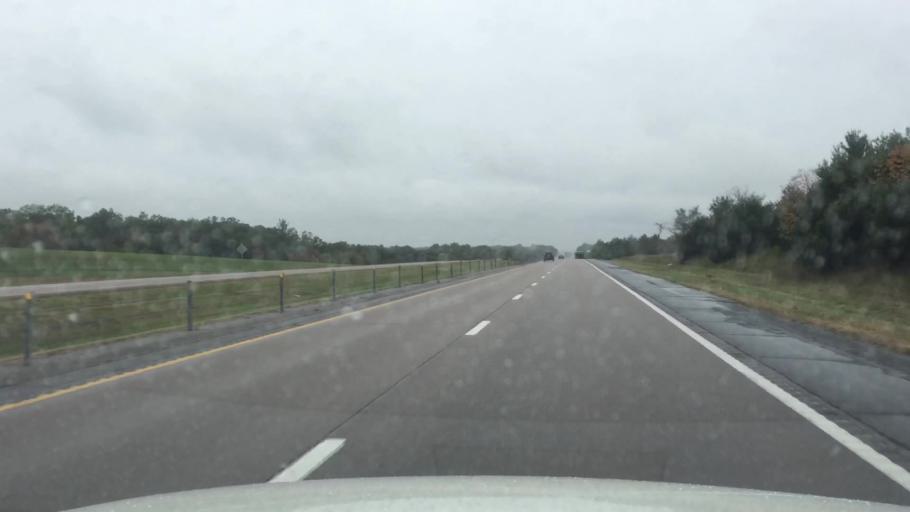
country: US
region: Missouri
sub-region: Boone County
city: Ashland
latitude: 38.7144
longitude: -92.2547
